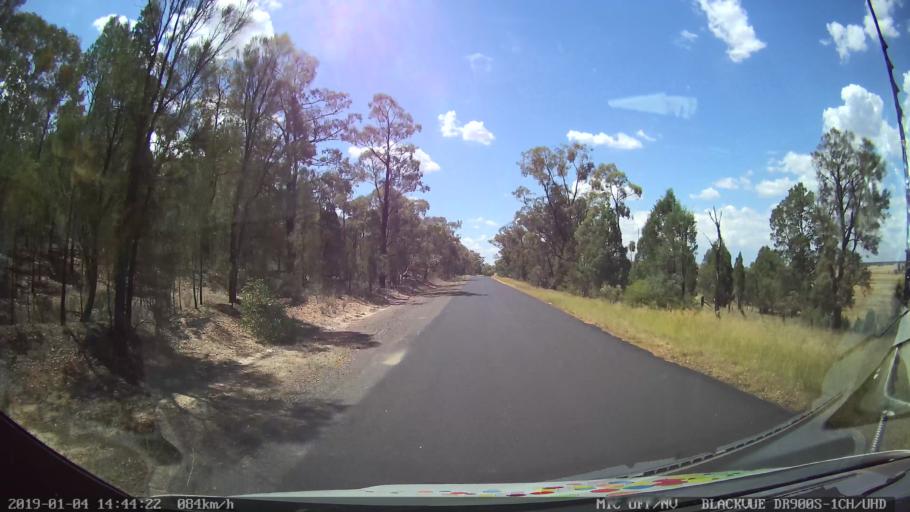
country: AU
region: New South Wales
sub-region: Dubbo Municipality
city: Dubbo
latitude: -32.1072
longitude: 148.6555
